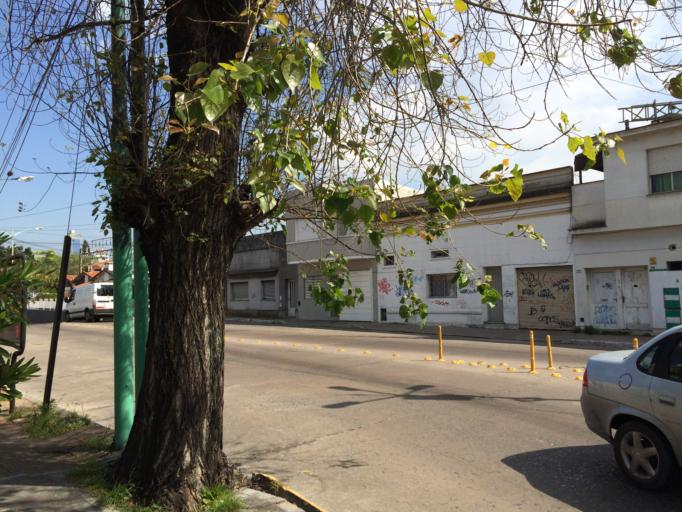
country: AR
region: Buenos Aires
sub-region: Partido de Lomas de Zamora
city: Lomas de Zamora
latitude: -34.7554
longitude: -58.3955
